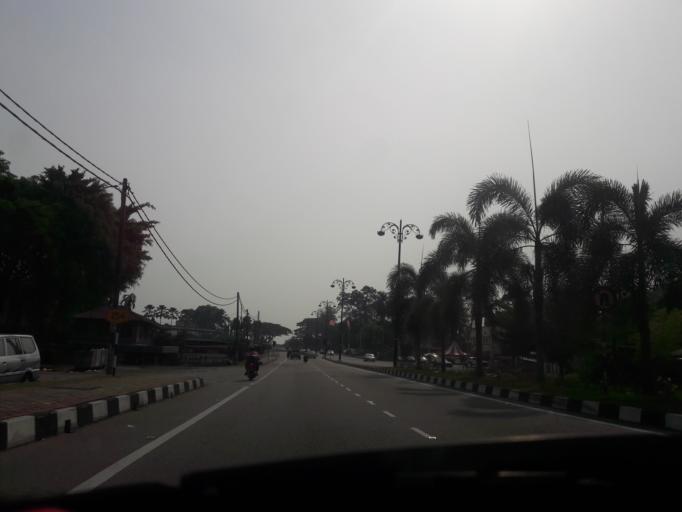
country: MY
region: Kedah
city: Kulim
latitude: 5.3635
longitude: 100.5499
